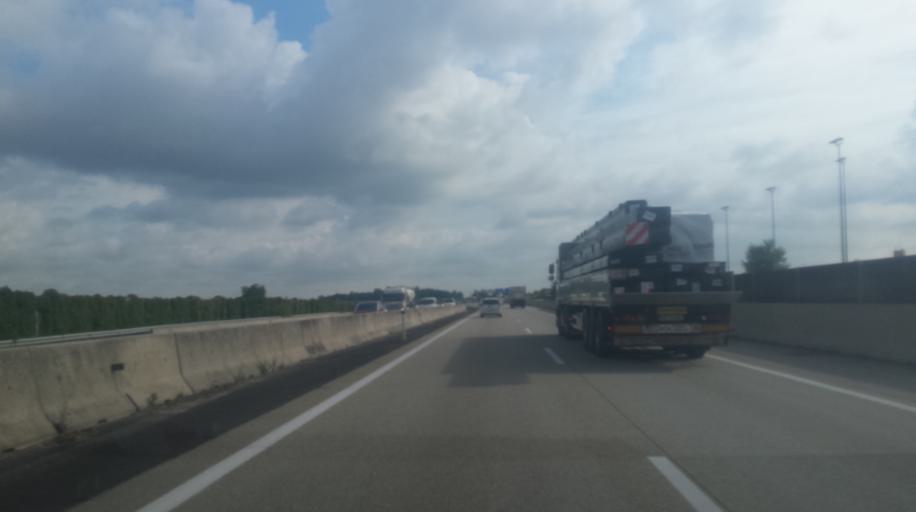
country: AT
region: Upper Austria
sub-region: Wels-Land
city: Sattledt
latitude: 48.0386
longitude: 13.9880
